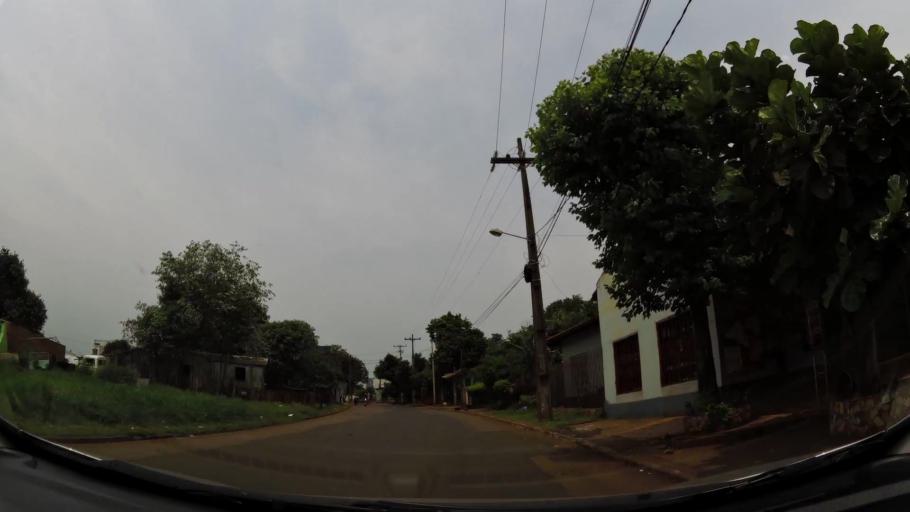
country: BR
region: Parana
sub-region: Foz Do Iguacu
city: Foz do Iguacu
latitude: -25.5649
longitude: -54.6113
